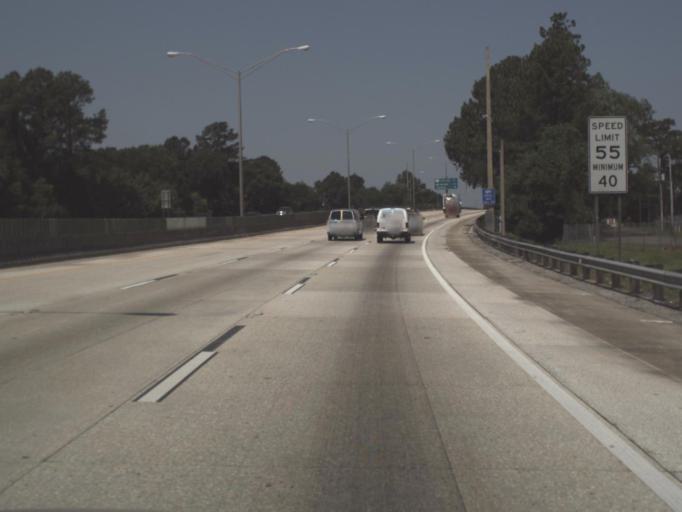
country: US
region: Florida
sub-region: Duval County
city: Jacksonville
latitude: 30.3158
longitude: -81.7407
